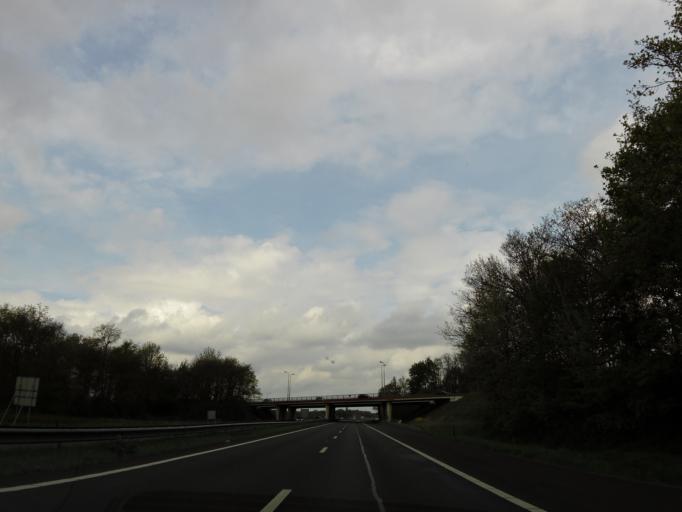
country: NL
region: Limburg
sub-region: Gemeente Leudal
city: Kelpen-Oler
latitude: 51.2342
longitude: 5.7954
